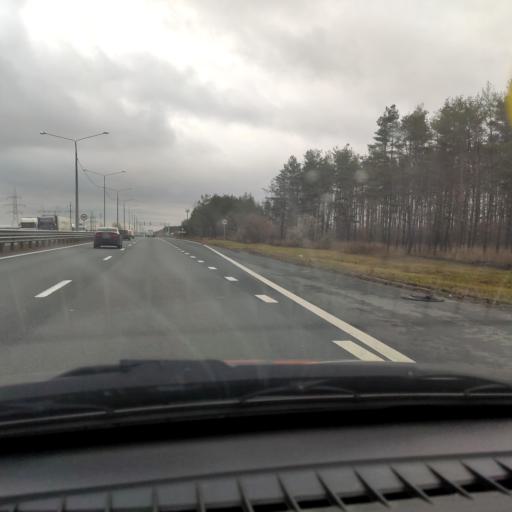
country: RU
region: Samara
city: Povolzhskiy
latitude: 53.5141
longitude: 49.6185
